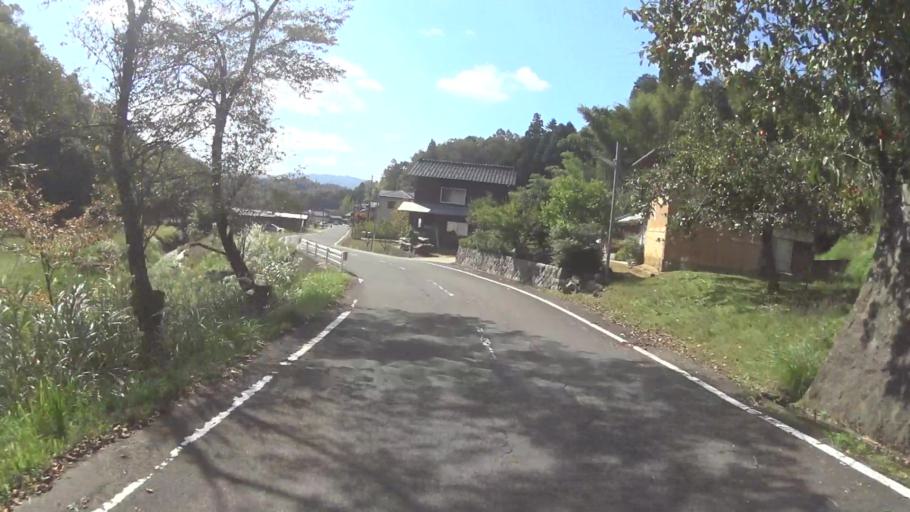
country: JP
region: Hyogo
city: Toyooka
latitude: 35.6044
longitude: 134.9861
